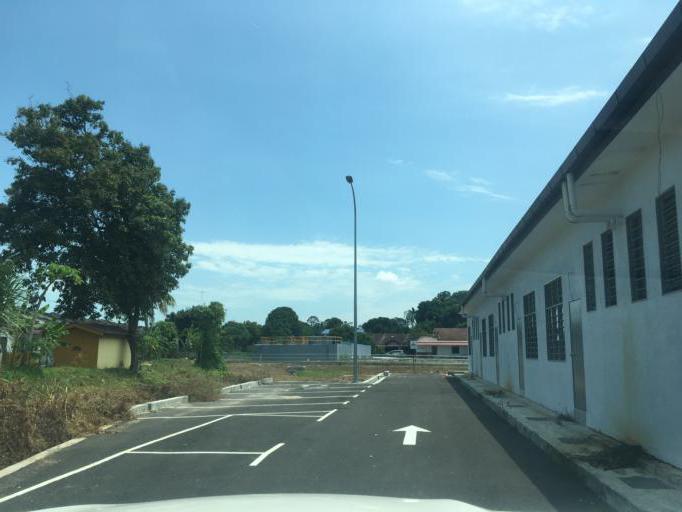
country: MY
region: Melaka
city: Kampung Ayer Molek
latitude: 2.2021
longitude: 102.3086
